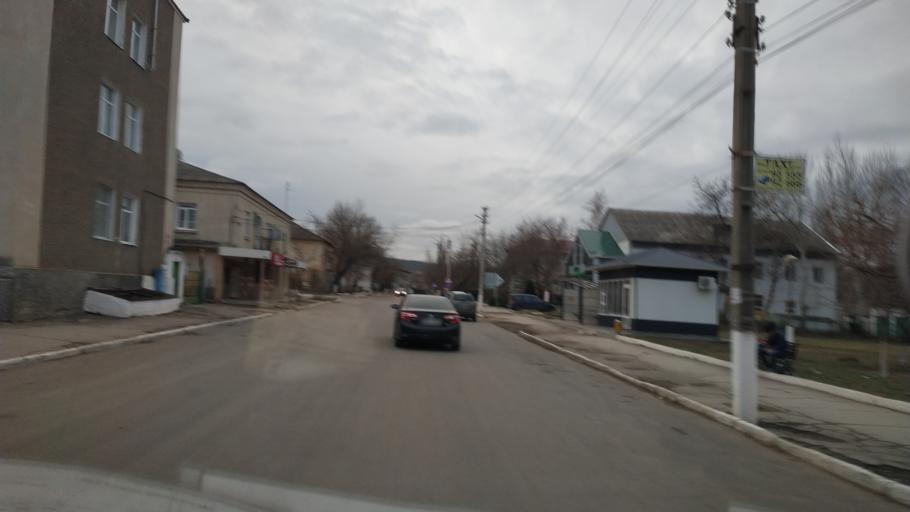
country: MD
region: Causeni
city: Causeni
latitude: 46.6397
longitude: 29.4062
